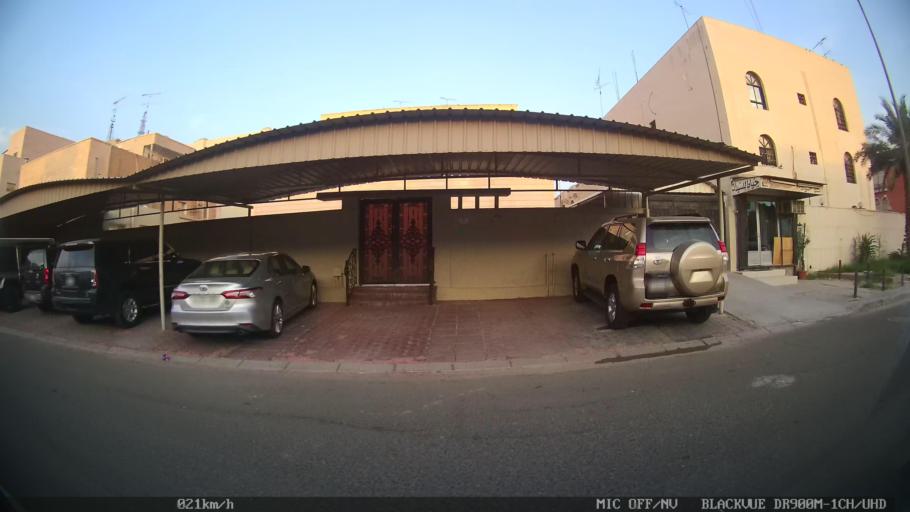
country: KW
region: Al Farwaniyah
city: Al Farwaniyah
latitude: 29.2993
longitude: 47.9785
